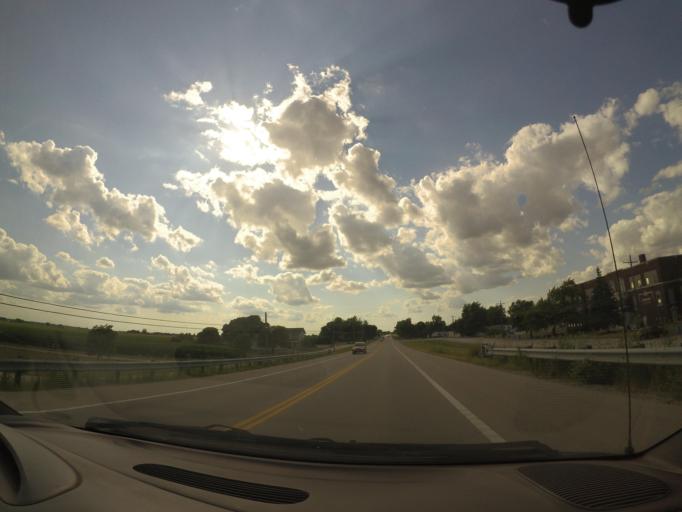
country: US
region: Ohio
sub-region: Wood County
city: Luckey
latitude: 41.4973
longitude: -83.4774
